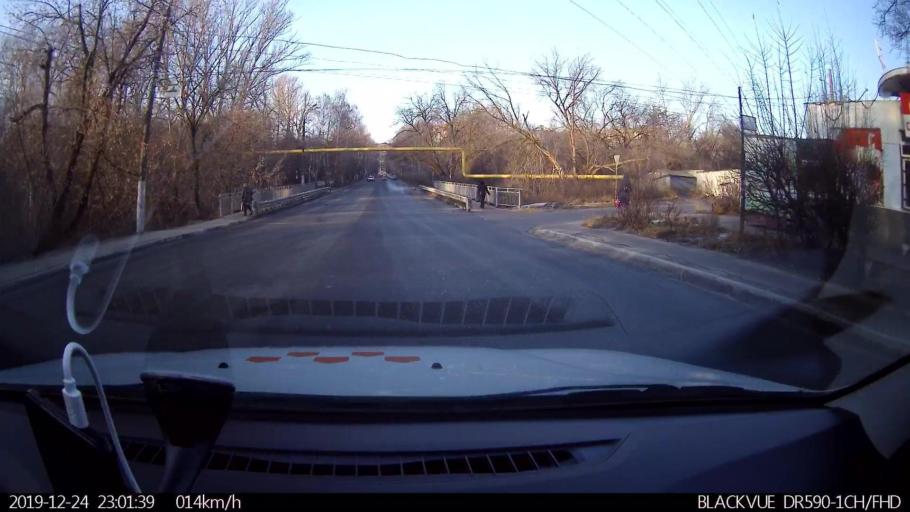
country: RU
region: Nizjnij Novgorod
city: Nizhniy Novgorod
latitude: 56.2679
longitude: 43.9255
